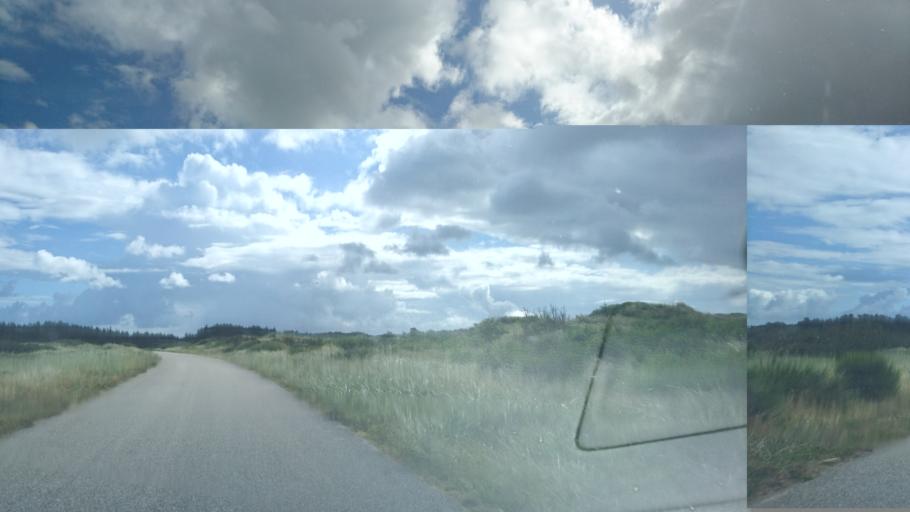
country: DK
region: North Denmark
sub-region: Frederikshavn Kommune
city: Skagen
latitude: 57.7197
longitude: 10.5165
